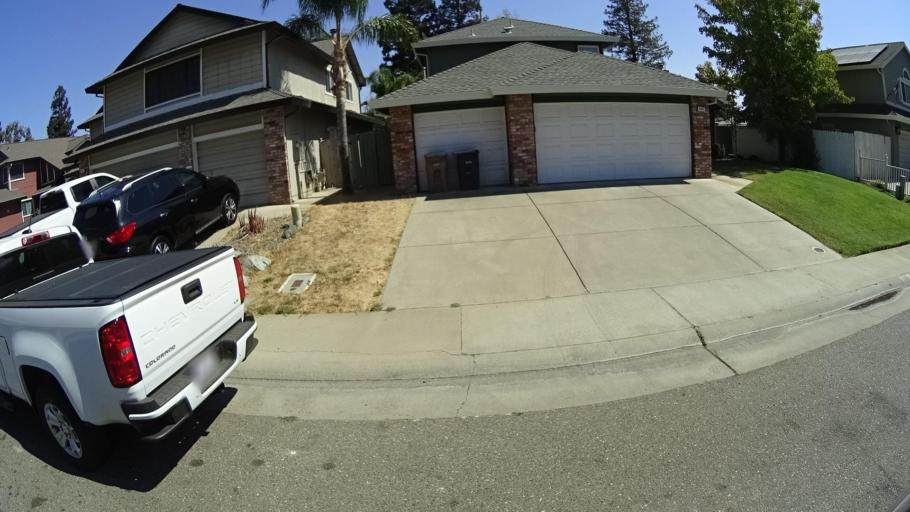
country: US
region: California
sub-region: Sacramento County
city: Laguna
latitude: 38.4137
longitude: -121.4150
